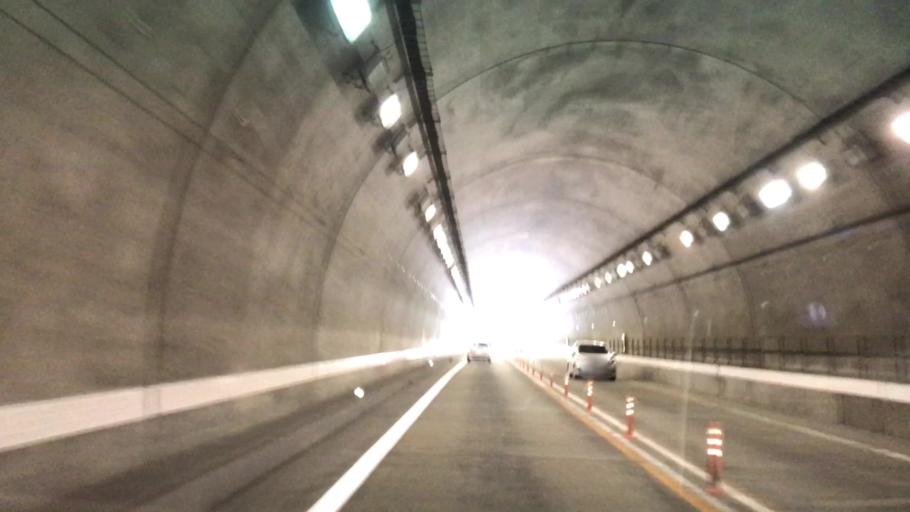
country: JP
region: Hokkaido
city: Shimo-furano
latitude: 42.9731
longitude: 142.3877
